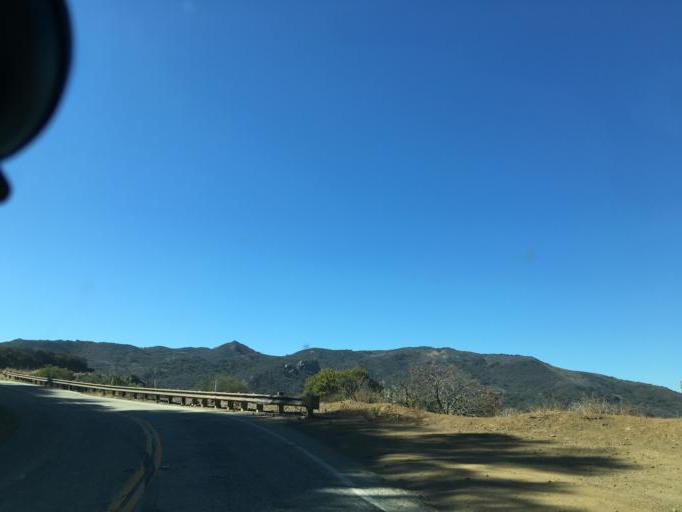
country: US
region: California
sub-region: Ventura County
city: Casa Conejo
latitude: 34.0899
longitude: -118.9028
